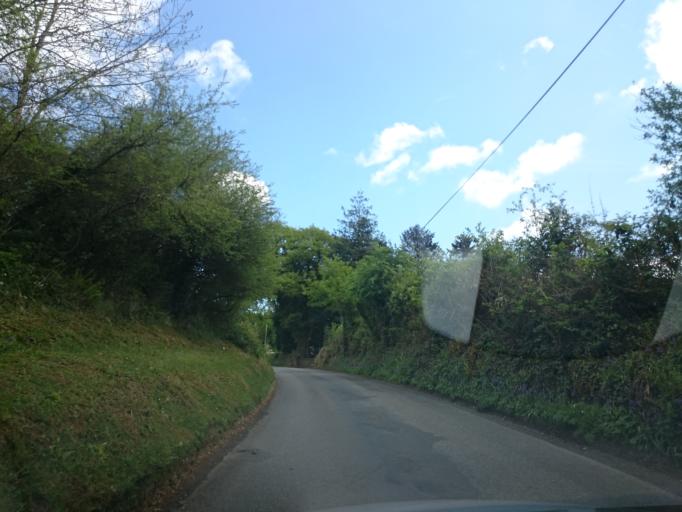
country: IE
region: Leinster
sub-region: Laois
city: Mountrath
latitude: 53.0317
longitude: -7.5622
